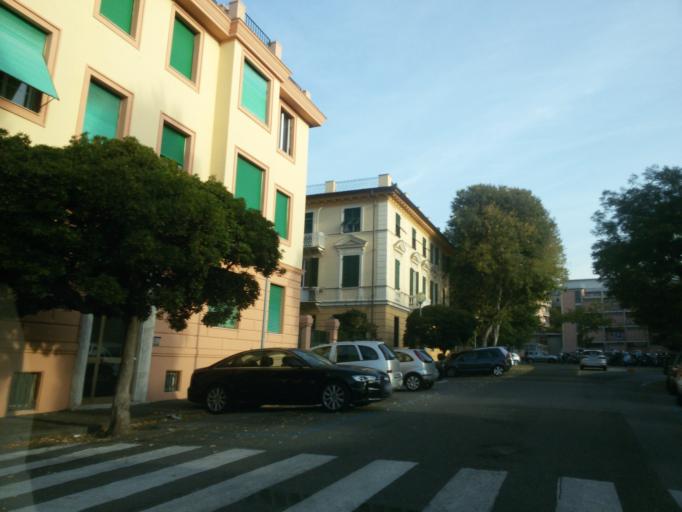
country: IT
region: Liguria
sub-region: Provincia di Genova
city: San Teodoro
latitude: 44.3982
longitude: 8.9391
